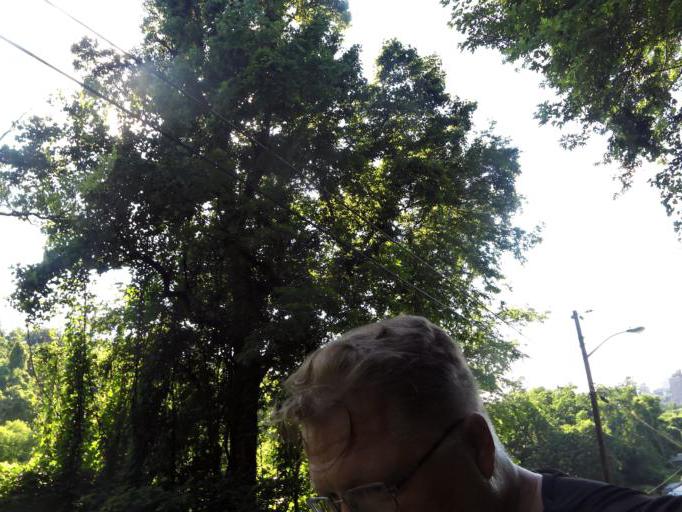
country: US
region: Tennessee
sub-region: Knox County
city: Knoxville
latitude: 35.9533
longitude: -83.9079
